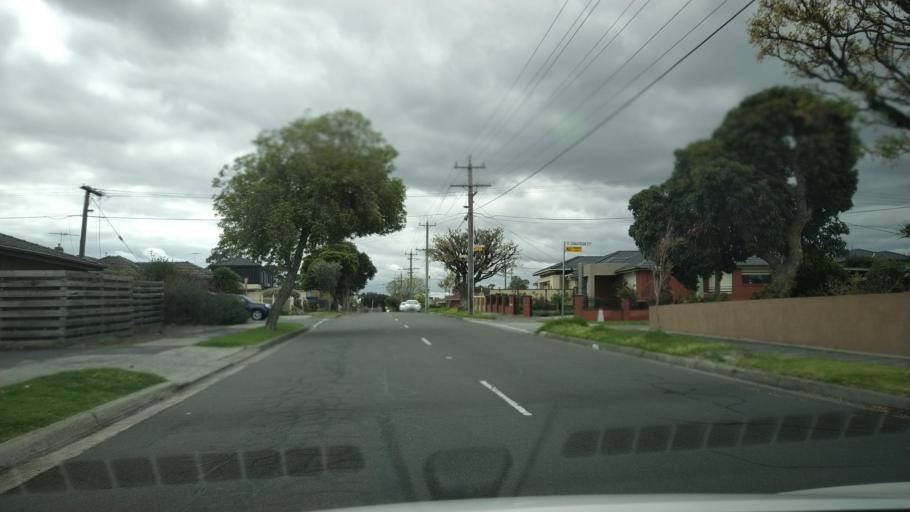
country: AU
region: Victoria
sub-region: Greater Dandenong
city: Noble Park
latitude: -37.9752
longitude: 145.1784
